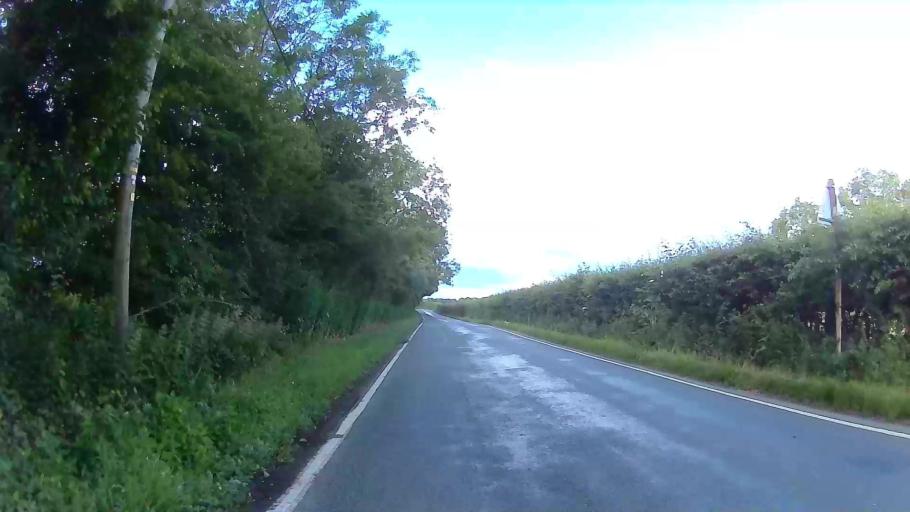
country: GB
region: England
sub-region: Essex
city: Kelvedon Hatch
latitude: 51.6453
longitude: 0.2384
